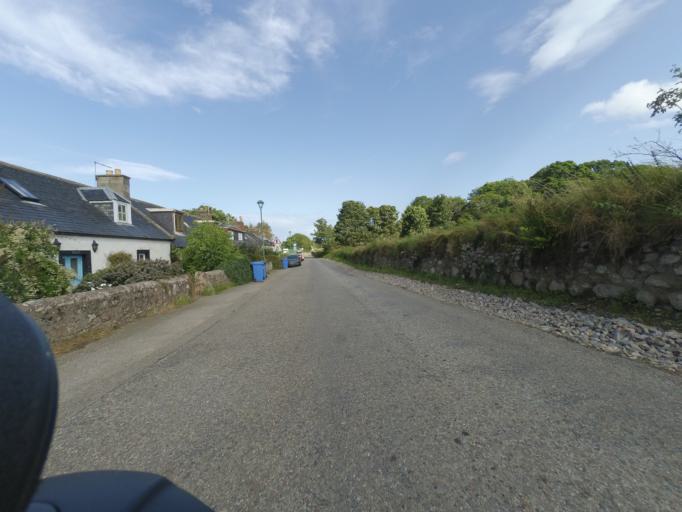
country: GB
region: Scotland
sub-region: Highland
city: Invergordon
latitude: 57.6583
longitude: -4.1463
